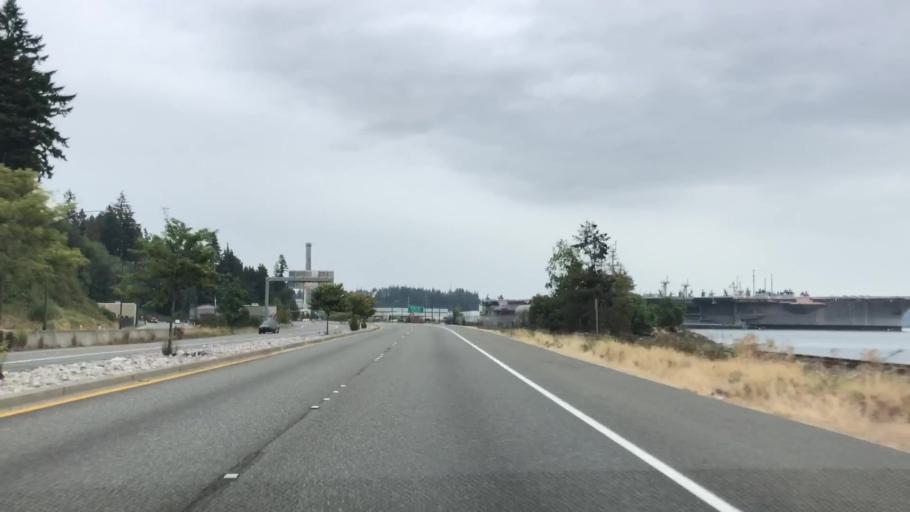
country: US
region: Washington
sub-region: Kitsap County
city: Navy Yard City
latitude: 47.5507
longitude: -122.6640
